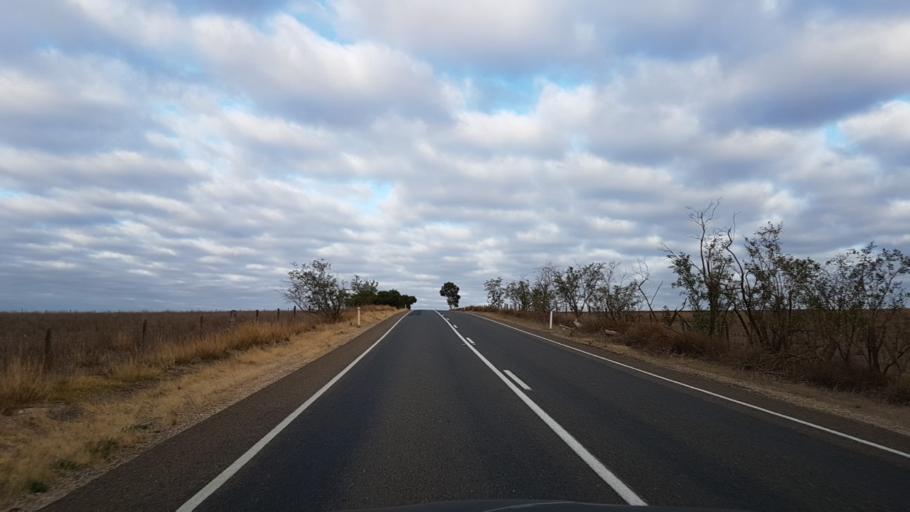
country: AU
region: South Australia
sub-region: Mount Barker
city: Callington
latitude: -35.1910
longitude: 138.9914
